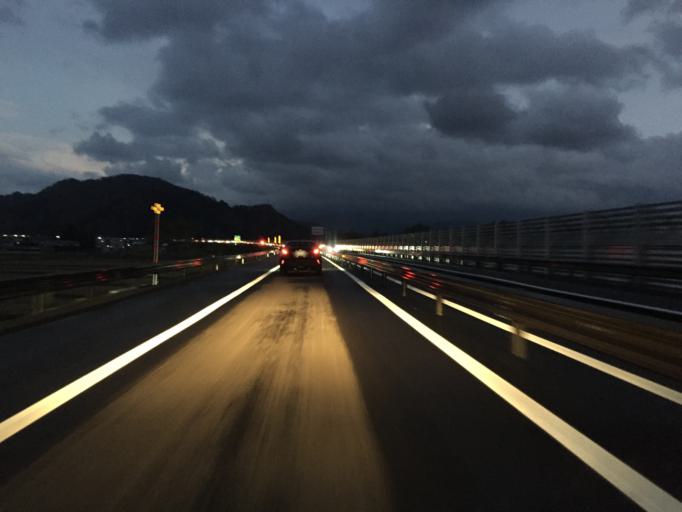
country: JP
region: Yamagata
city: Yonezawa
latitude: 37.9043
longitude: 140.1434
